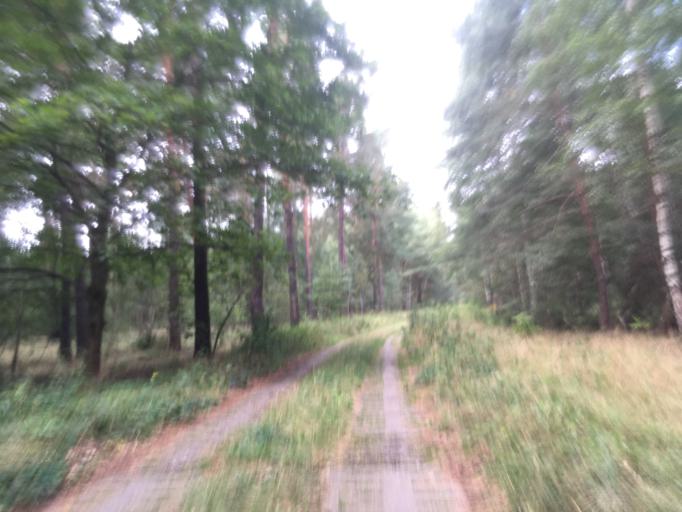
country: DE
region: Berlin
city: Schmockwitz
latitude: 52.3433
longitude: 13.6717
